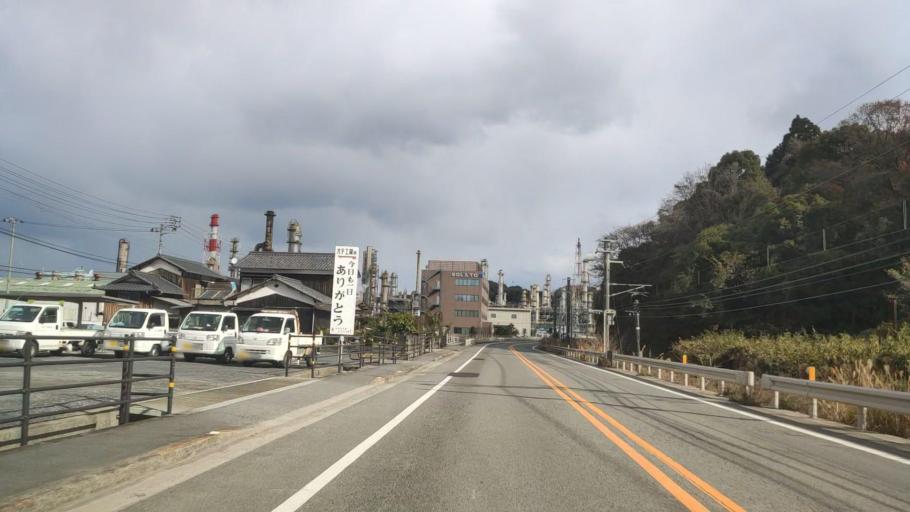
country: JP
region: Ehime
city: Hojo
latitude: 34.0461
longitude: 132.8572
